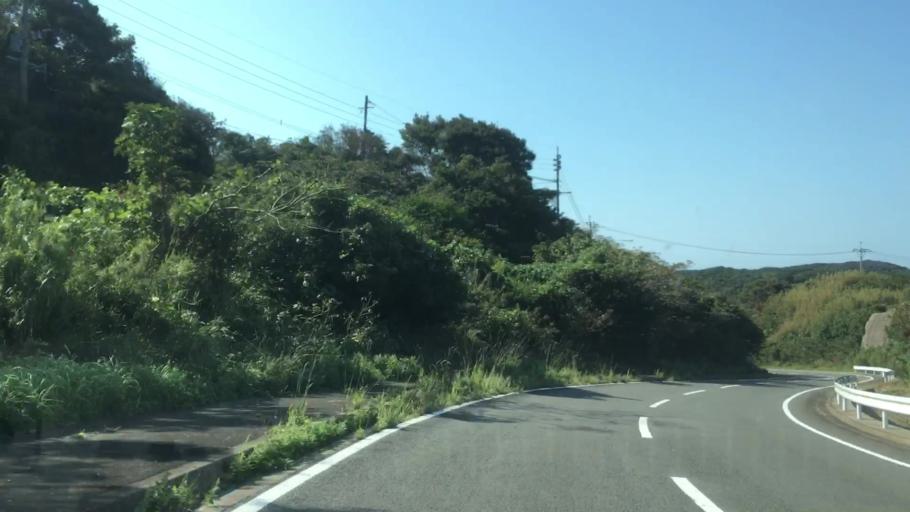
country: JP
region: Nagasaki
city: Sasebo
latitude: 33.0101
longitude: 129.5678
